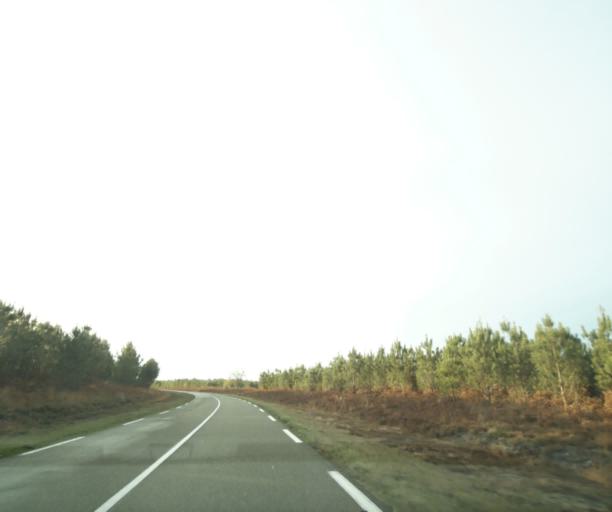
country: FR
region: Aquitaine
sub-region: Departement des Landes
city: Gabarret
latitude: 44.0870
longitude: -0.0784
